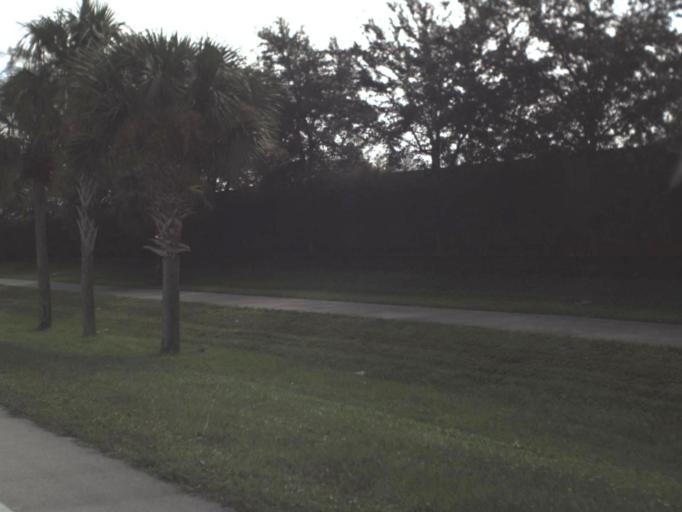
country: US
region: Florida
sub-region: Lee County
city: Fort Myers Shores
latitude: 26.7063
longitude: -81.7381
